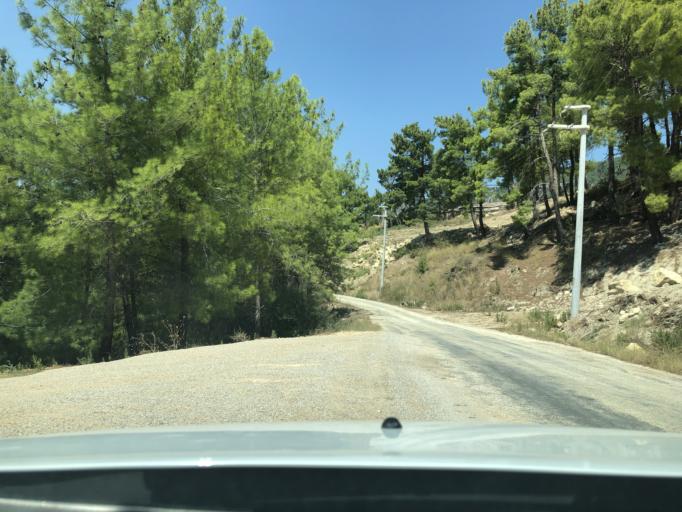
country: TR
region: Antalya
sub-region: Manavgat
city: Manavgat
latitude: 36.8706
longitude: 31.5536
